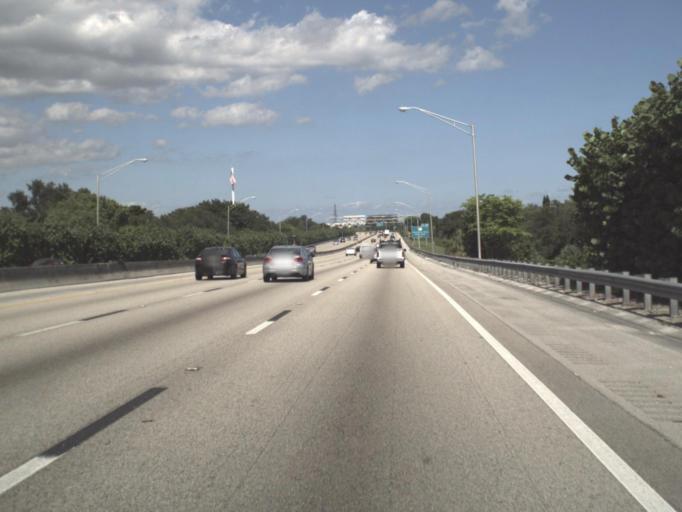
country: US
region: Florida
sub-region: Broward County
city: Pembroke Pines
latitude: 25.9961
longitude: -80.2233
